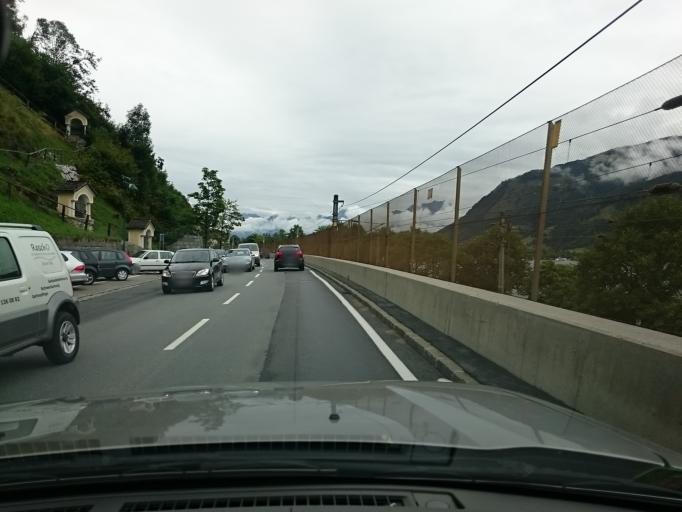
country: AT
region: Salzburg
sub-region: Politischer Bezirk Zell am See
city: Zell am See
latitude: 47.3304
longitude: 12.7968
